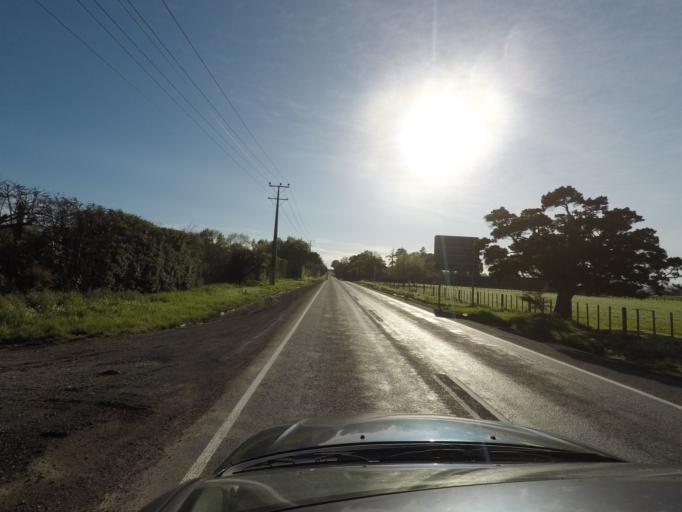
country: NZ
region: Auckland
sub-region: Auckland
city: Papakura
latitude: -37.0158
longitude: 174.9416
